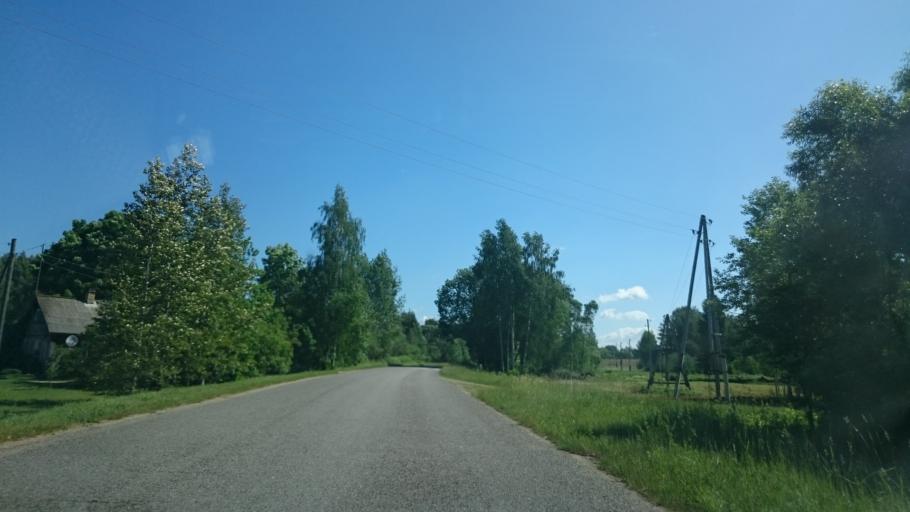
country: LV
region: Ludzas Rajons
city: Ludza
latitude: 56.5130
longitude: 27.7923
